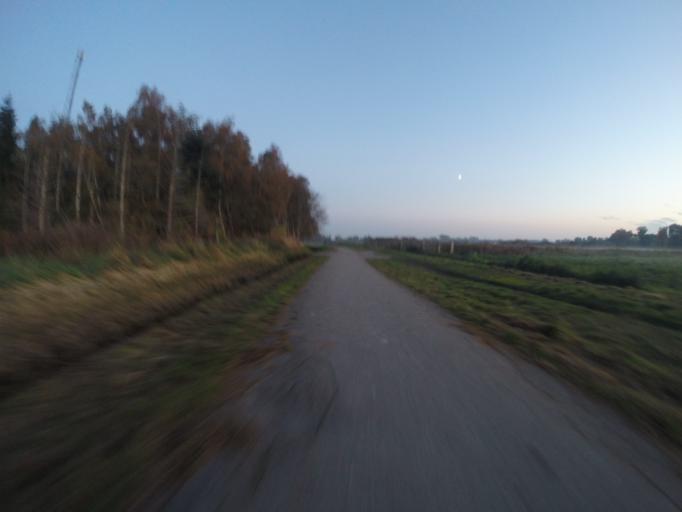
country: DK
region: Capital Region
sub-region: Vallensbaek Kommune
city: Vallensbaek
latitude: 55.6369
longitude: 12.3551
